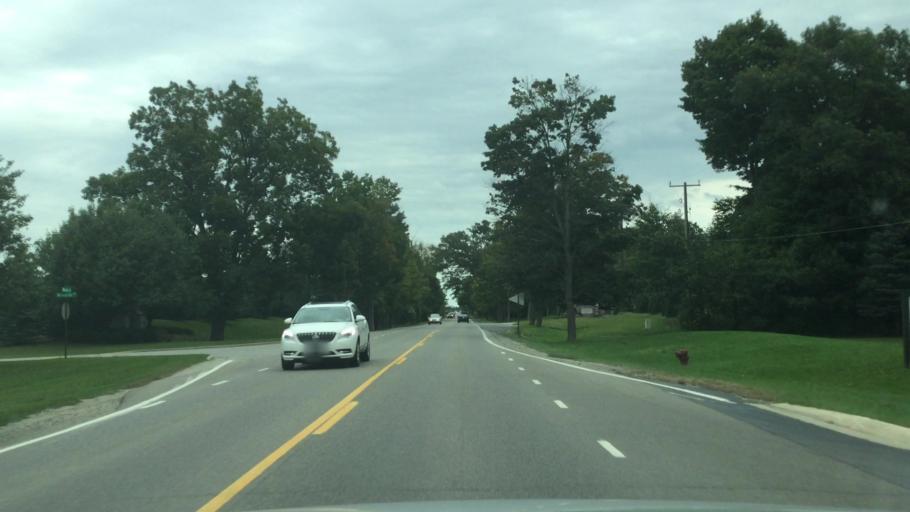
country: US
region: Michigan
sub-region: Livingston County
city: Whitmore Lake
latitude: 42.4639
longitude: -83.7721
